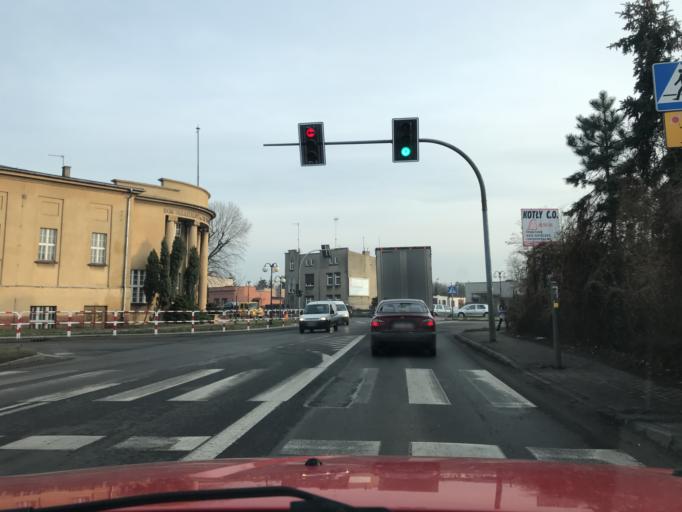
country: PL
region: Greater Poland Voivodeship
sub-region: Powiat pleszewski
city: Pleszew
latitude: 51.8987
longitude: 17.7887
